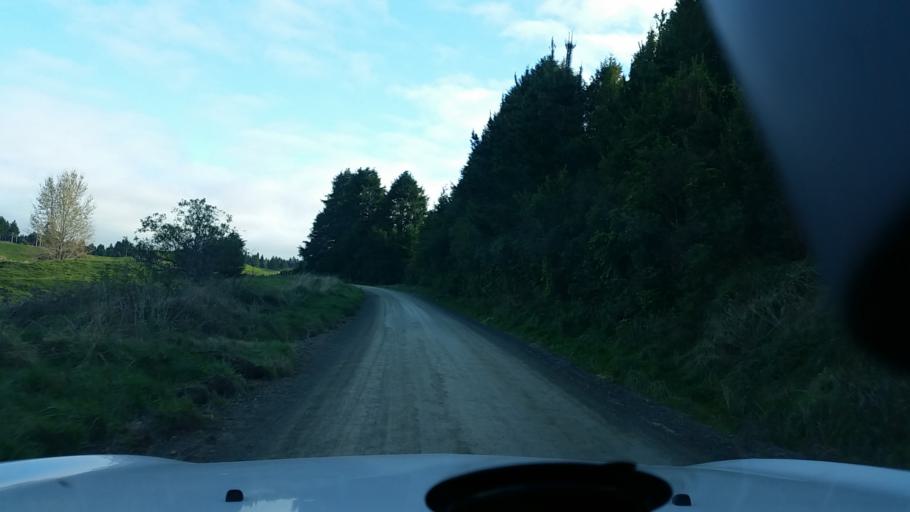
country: NZ
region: Hawke's Bay
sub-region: Napier City
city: Napier
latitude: -39.2598
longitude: 176.8461
